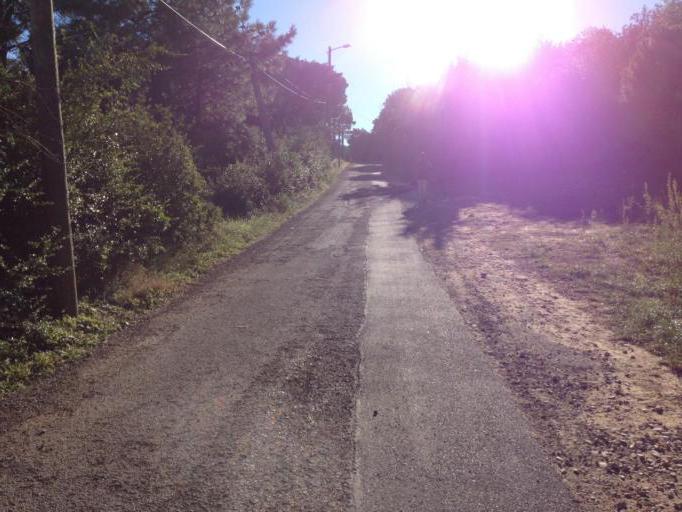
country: FR
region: Provence-Alpes-Cote d'Azur
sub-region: Departement du Vaucluse
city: Orange
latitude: 44.1222
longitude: 4.8094
